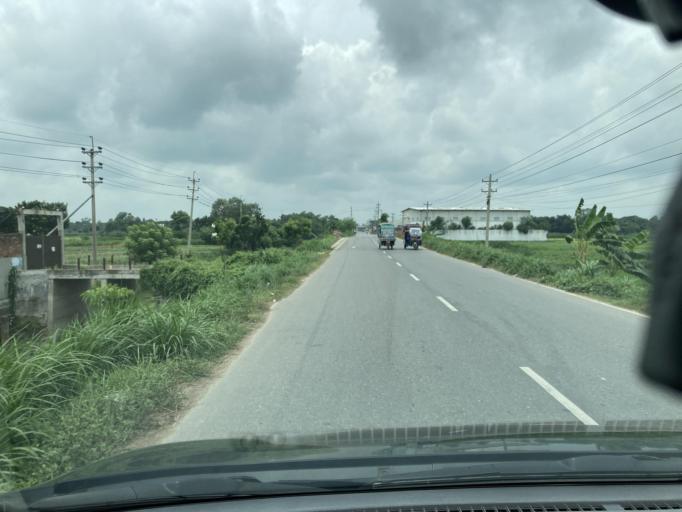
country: BD
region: Dhaka
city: Azimpur
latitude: 23.8062
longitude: 90.1966
